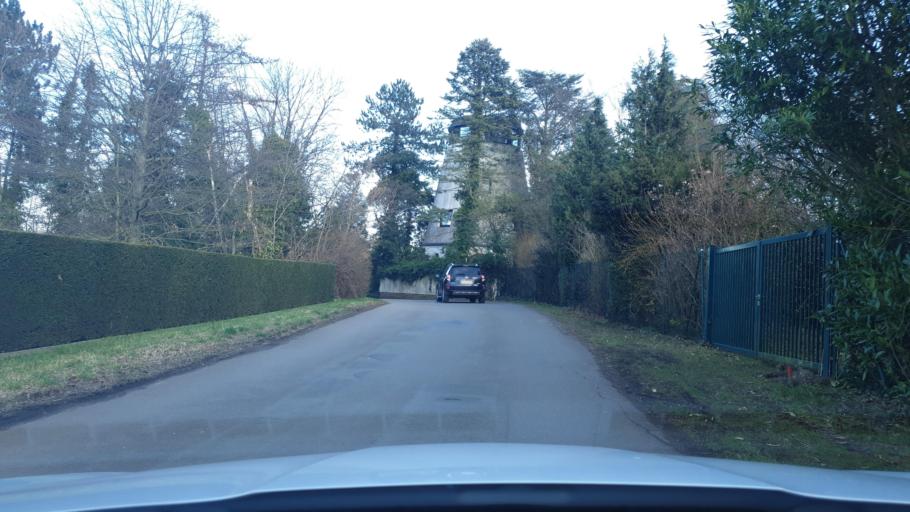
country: DE
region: North Rhine-Westphalia
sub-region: Regierungsbezirk Detmold
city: Minden
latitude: 52.2683
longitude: 8.8775
